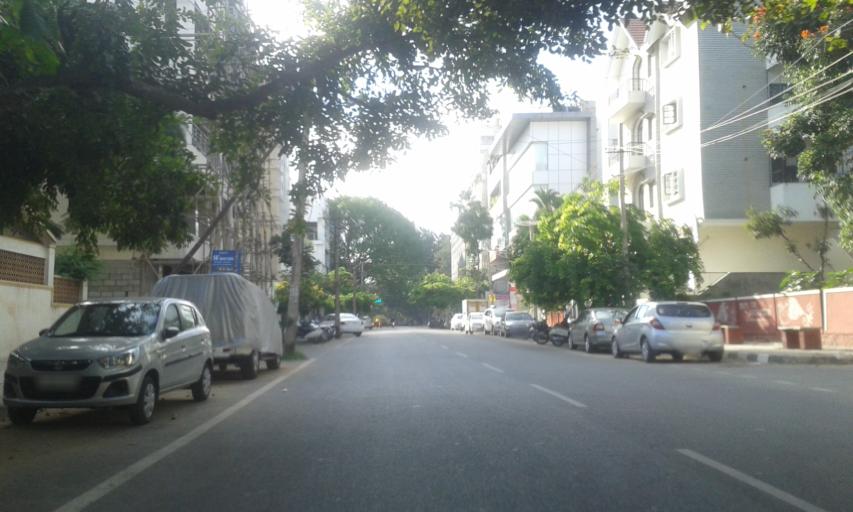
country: IN
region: Karnataka
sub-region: Bangalore Urban
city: Bangalore
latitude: 12.9263
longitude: 77.5875
